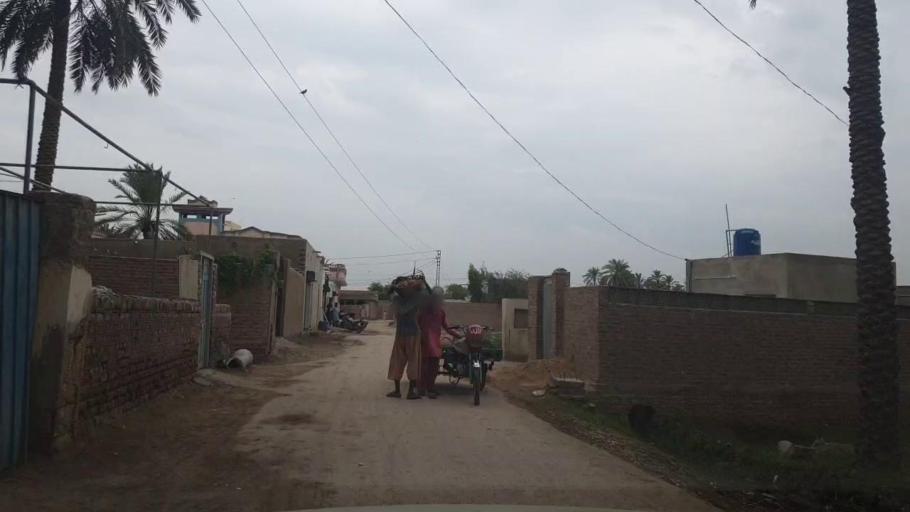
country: PK
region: Sindh
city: Khairpur
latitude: 27.5553
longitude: 68.7506
